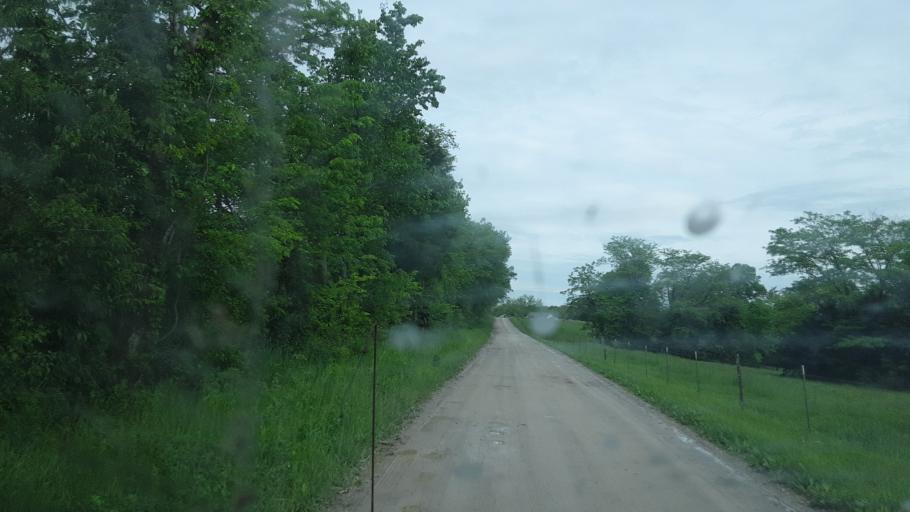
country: US
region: Missouri
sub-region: Clark County
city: Kahoka
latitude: 40.4249
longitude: -91.6084
